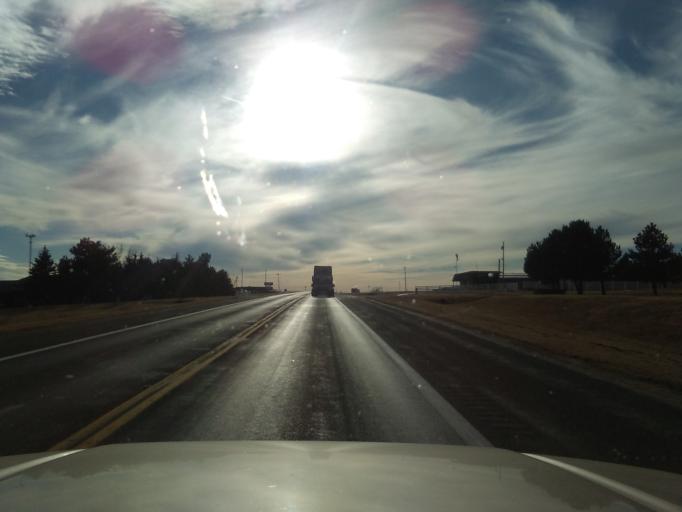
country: US
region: Kansas
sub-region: Norton County
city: Norton
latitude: 39.8327
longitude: -99.9056
